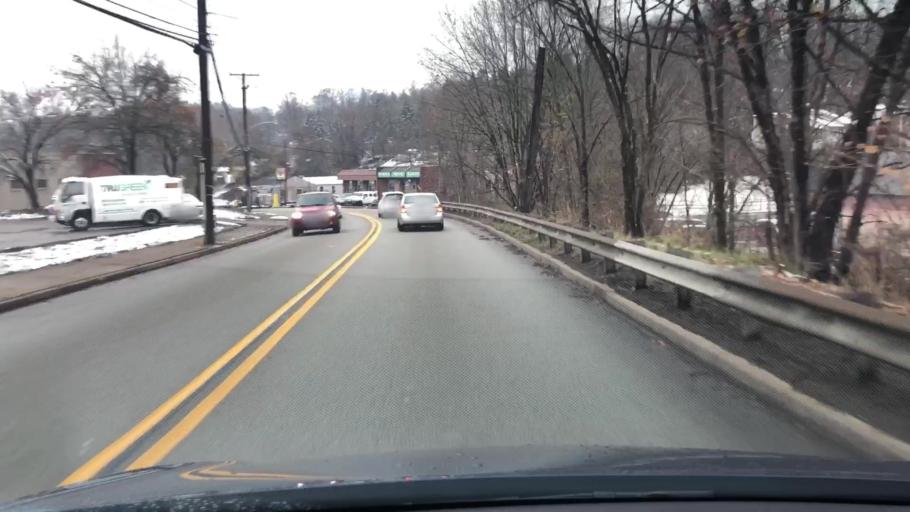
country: US
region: Pennsylvania
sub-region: Allegheny County
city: Churchill
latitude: 40.4532
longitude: -79.8254
